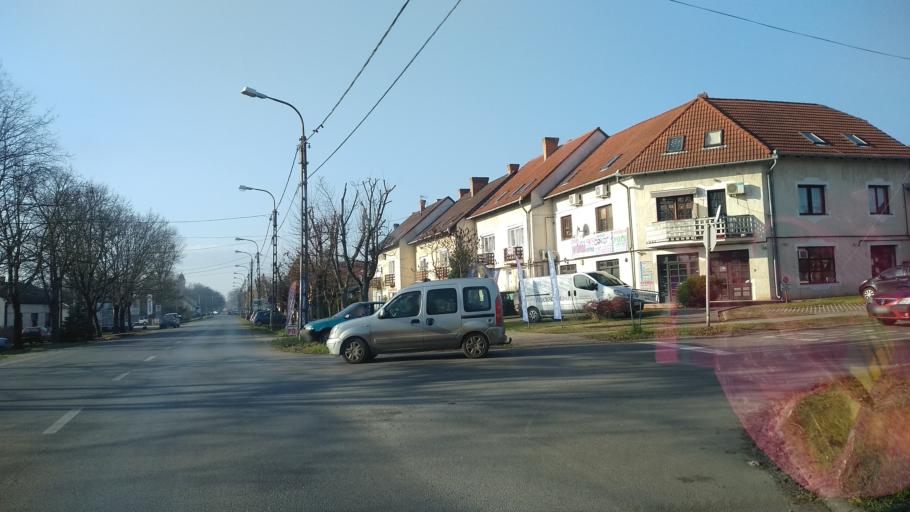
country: HU
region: Somogy
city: Barcs
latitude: 45.9594
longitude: 17.4720
